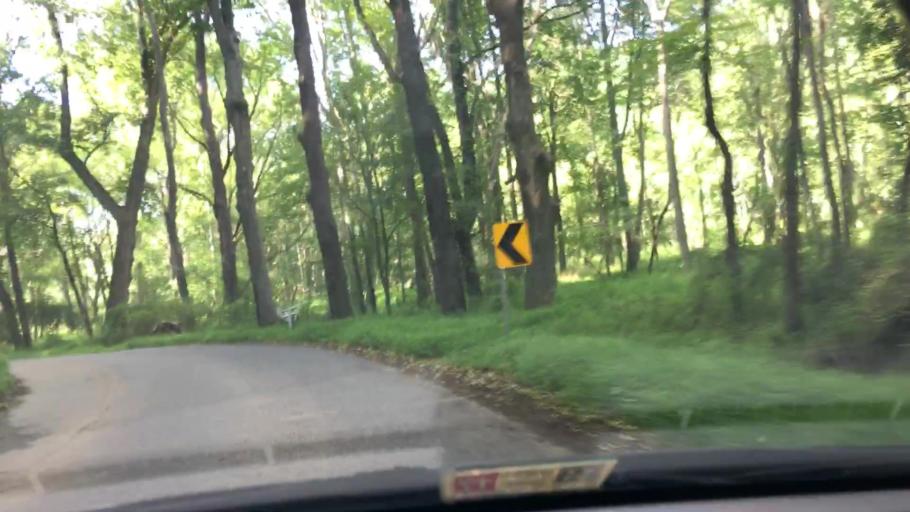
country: US
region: Maryland
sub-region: Montgomery County
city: Montgomery Village
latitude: 39.2122
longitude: -77.2048
